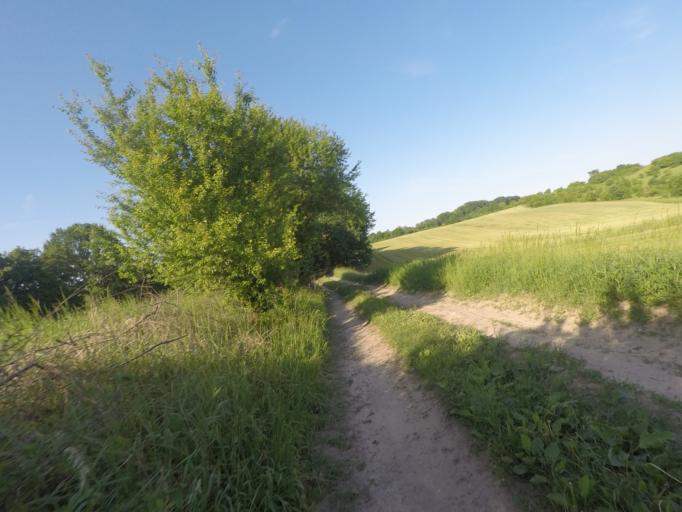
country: DE
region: Brandenburg
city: Marienwerder
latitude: 52.8715
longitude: 13.6898
